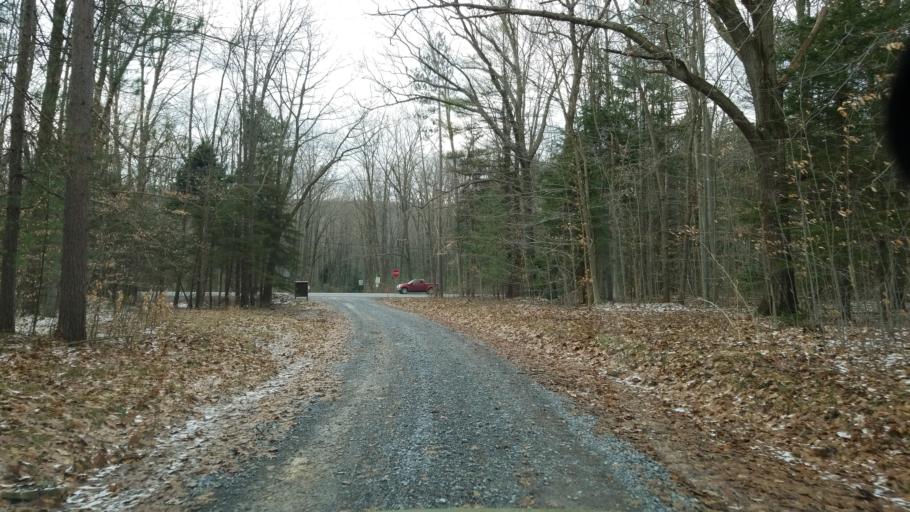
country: US
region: Pennsylvania
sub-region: Clearfield County
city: Clearfield
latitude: 41.1411
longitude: -78.5415
